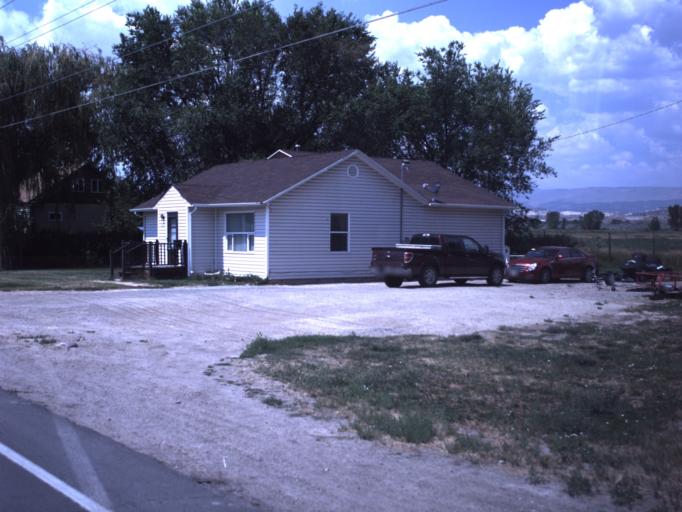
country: US
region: Utah
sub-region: Uintah County
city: Vernal
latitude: 40.4629
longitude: -109.5401
